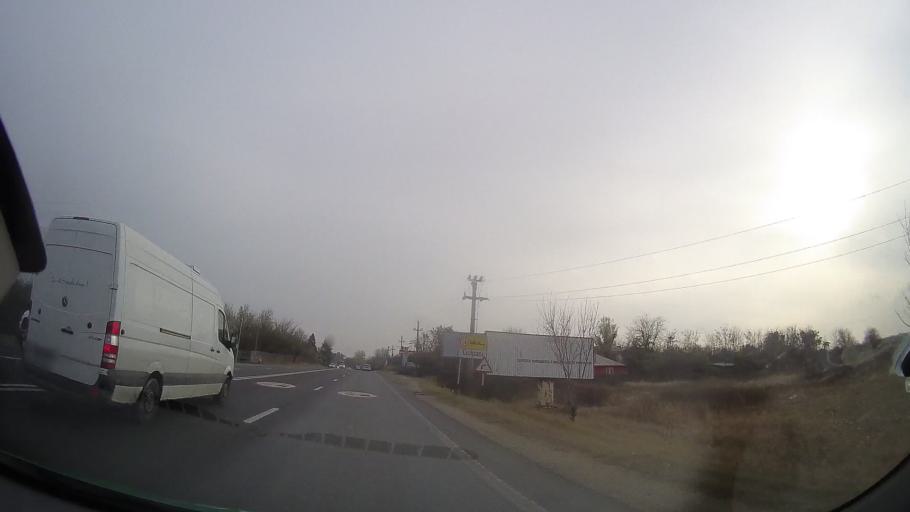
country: RO
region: Ilfov
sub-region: Comuna Ciolpani
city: Ciolpani
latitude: 44.7456
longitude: 26.1096
